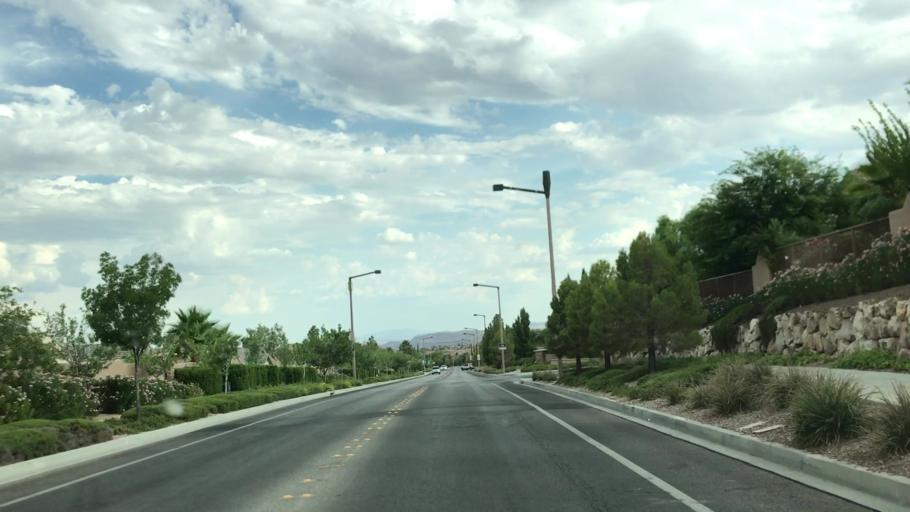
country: US
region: Nevada
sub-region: Clark County
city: Summerlin South
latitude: 36.1671
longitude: -115.3501
